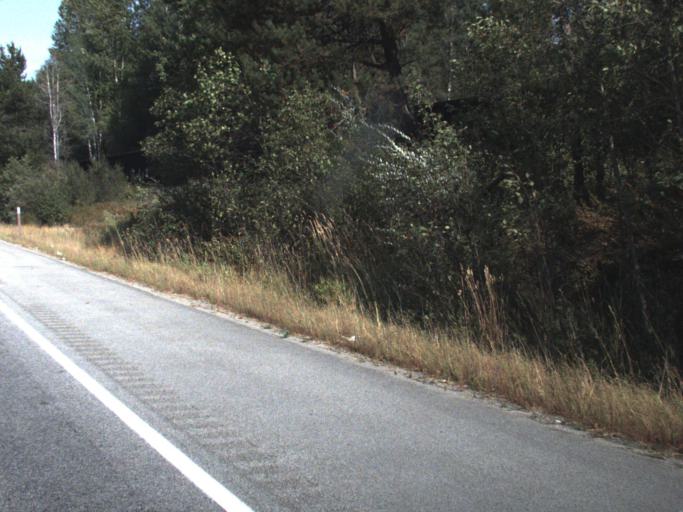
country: US
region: Washington
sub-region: Pend Oreille County
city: Newport
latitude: 48.1695
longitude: -117.0756
